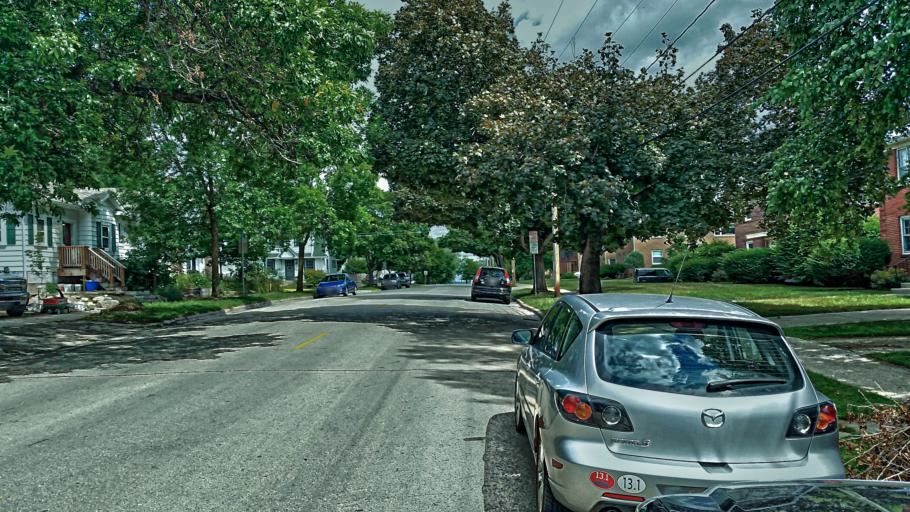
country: US
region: Wisconsin
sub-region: Dane County
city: Madison
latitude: 43.0570
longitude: -89.4032
